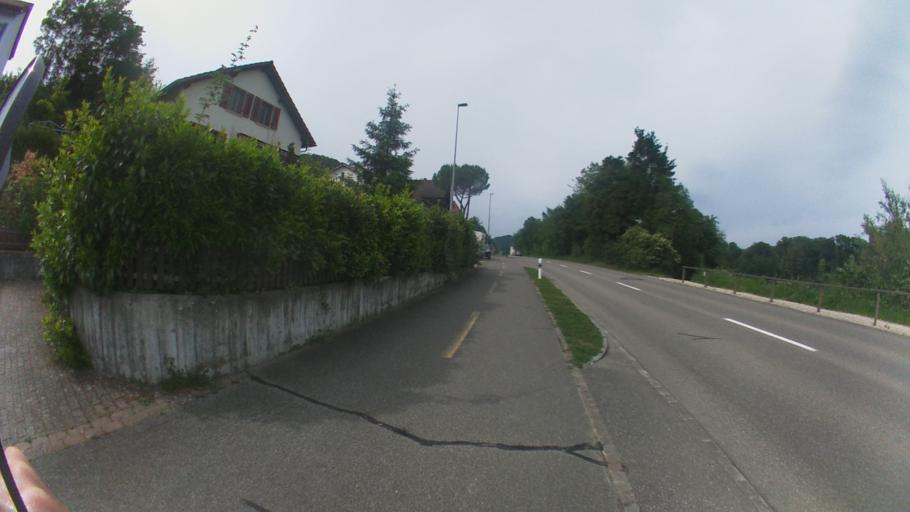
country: CH
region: Aargau
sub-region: Bezirk Zurzach
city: Koblenz
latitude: 47.5997
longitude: 8.2195
